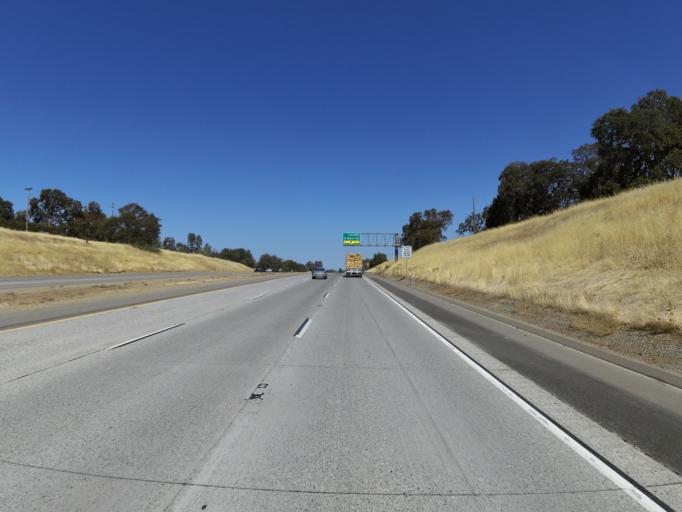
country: US
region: California
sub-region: Tehama County
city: Red Bluff
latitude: 40.1415
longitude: -122.2213
